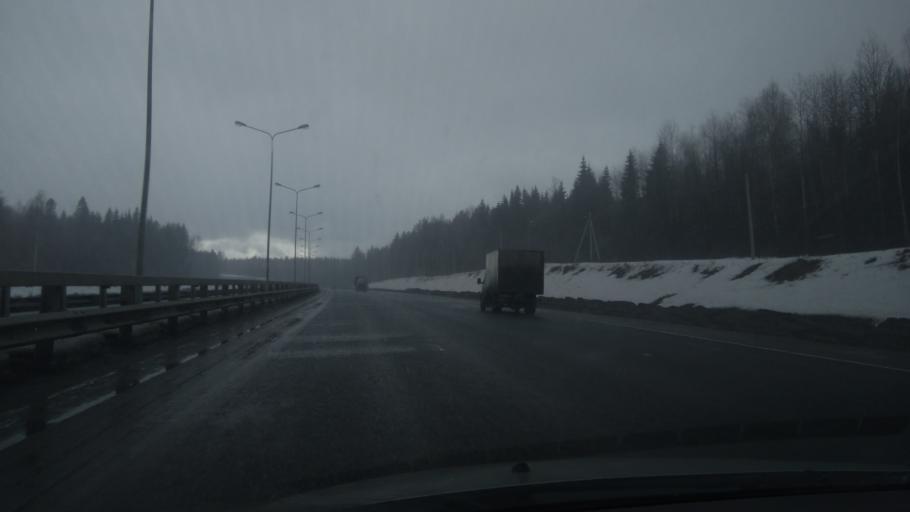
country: RU
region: Perm
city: Zvezdnyy
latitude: 57.7529
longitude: 56.3328
